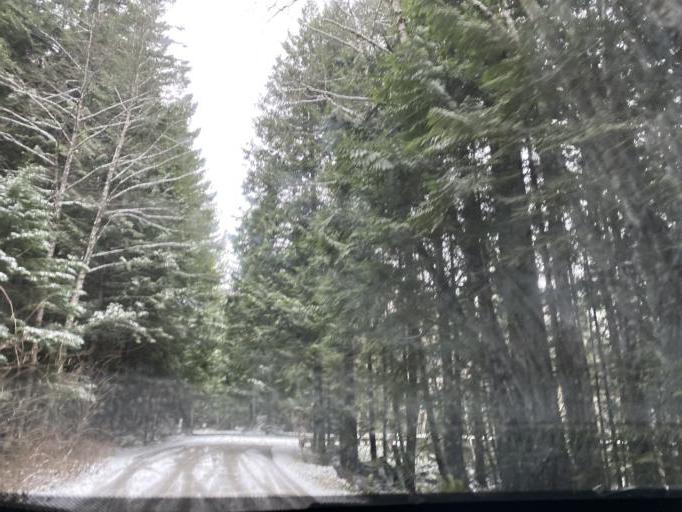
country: US
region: Washington
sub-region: King County
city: Tanner
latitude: 47.3931
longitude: -121.4811
